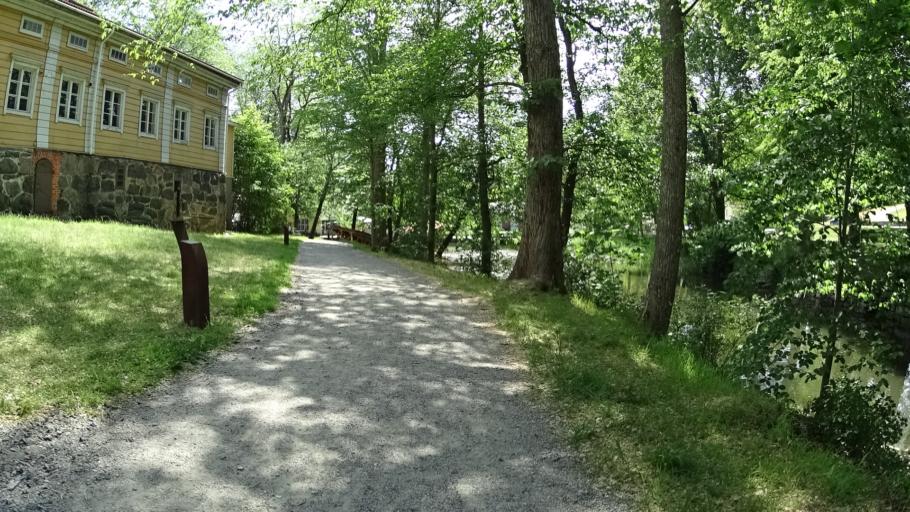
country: FI
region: Uusimaa
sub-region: Raaseporin
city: Pohja
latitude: 60.1285
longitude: 23.5417
